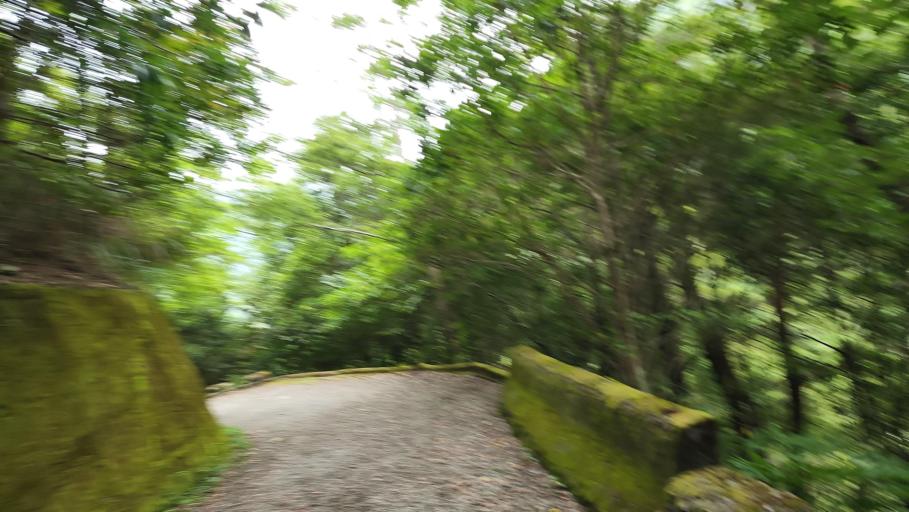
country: TW
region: Taiwan
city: Daxi
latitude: 24.7107
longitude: 121.4348
